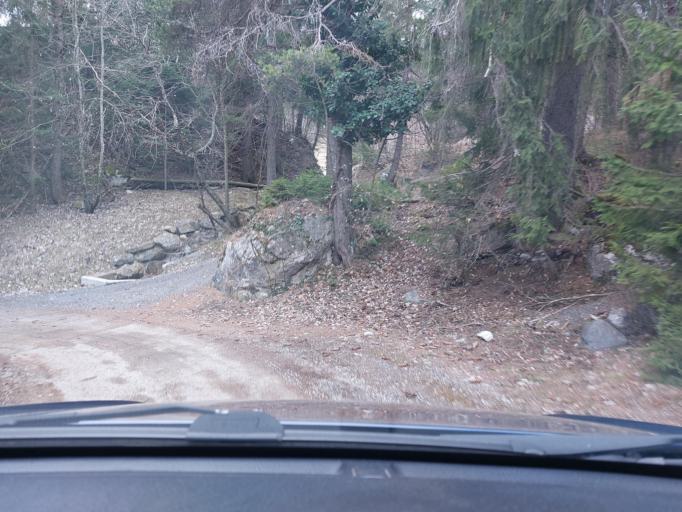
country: CH
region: Valais
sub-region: Sion District
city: Saviese
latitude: 46.2717
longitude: 7.3176
